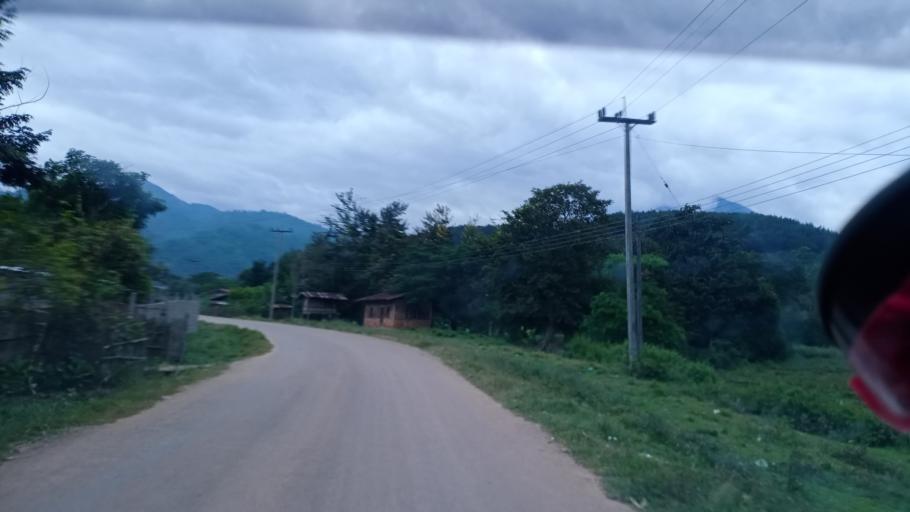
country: TH
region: Changwat Bueng Kan
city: Pak Khat
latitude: 18.7098
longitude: 103.2111
